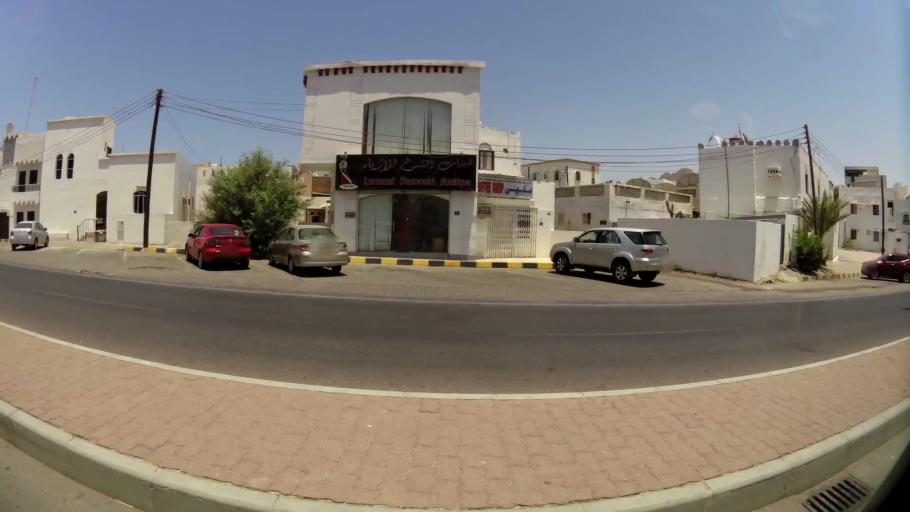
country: OM
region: Muhafazat Masqat
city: Muscat
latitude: 23.6254
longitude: 58.5594
